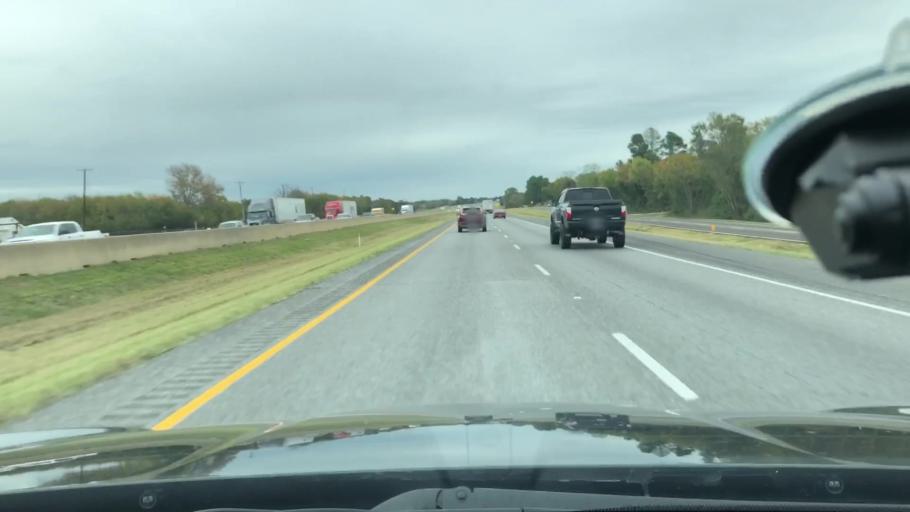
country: US
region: Texas
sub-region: Hunt County
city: Greenville
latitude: 33.1329
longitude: -96.0288
